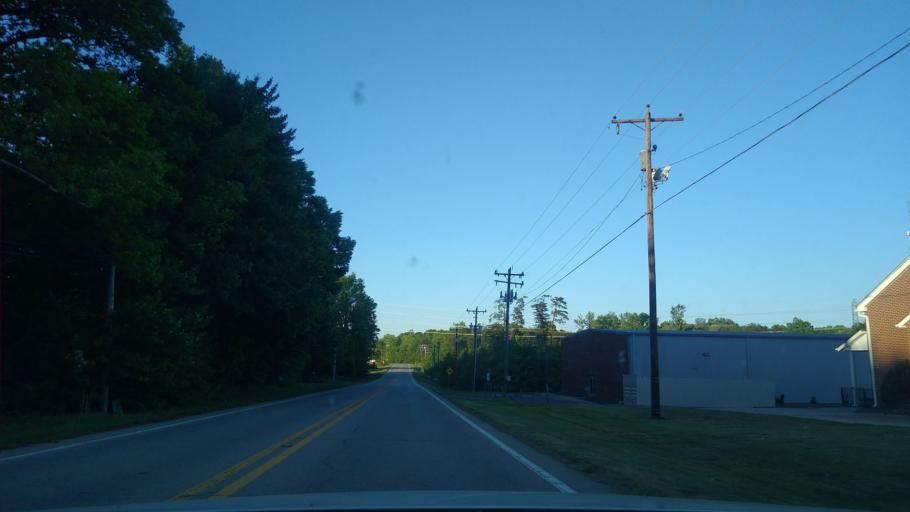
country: US
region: North Carolina
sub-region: Rockingham County
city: Reidsville
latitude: 36.3624
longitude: -79.6201
